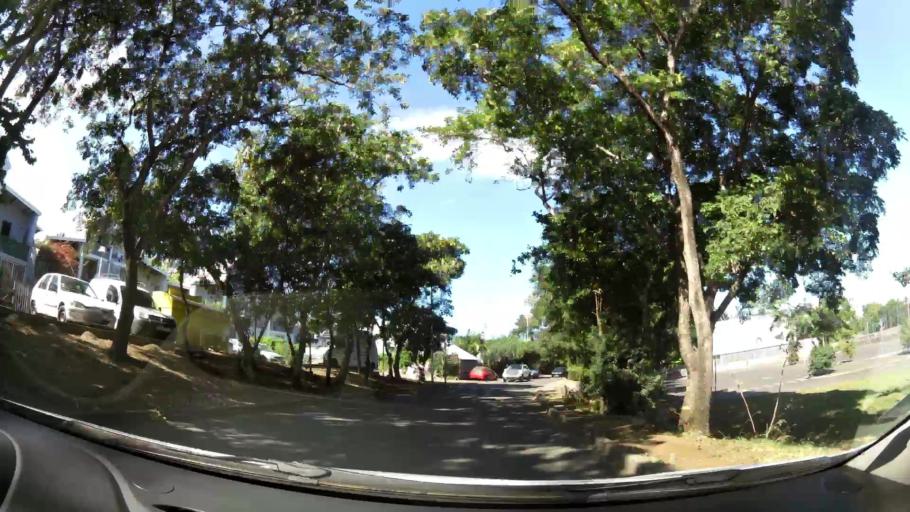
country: RE
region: Reunion
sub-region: Reunion
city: Saint-Pierre
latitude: -21.3253
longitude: 55.4766
